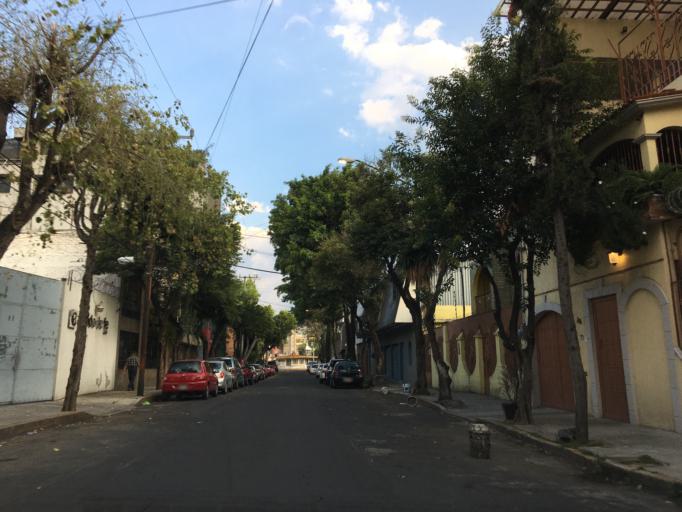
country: MX
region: Mexico City
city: Cuauhtemoc
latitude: 19.4633
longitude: -99.1462
